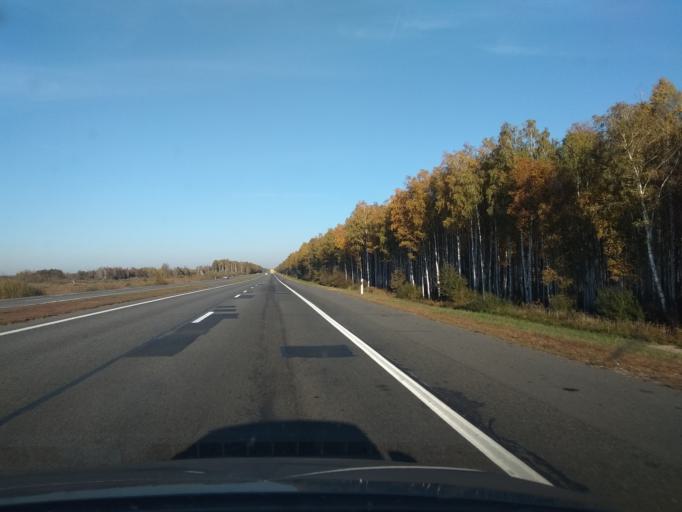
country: BY
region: Brest
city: Nyakhachava
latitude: 52.6114
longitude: 25.1757
